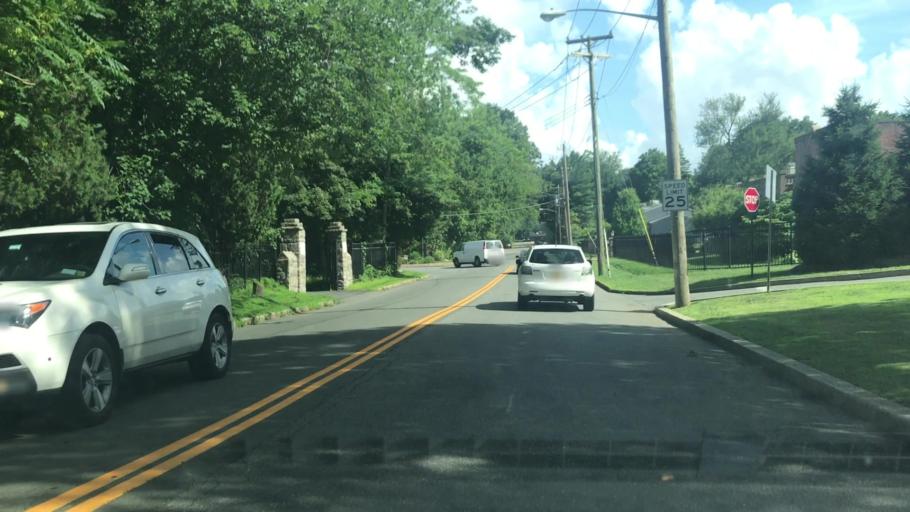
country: US
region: New York
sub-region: Westchester County
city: Tuckahoe
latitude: 40.9653
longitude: -73.8085
